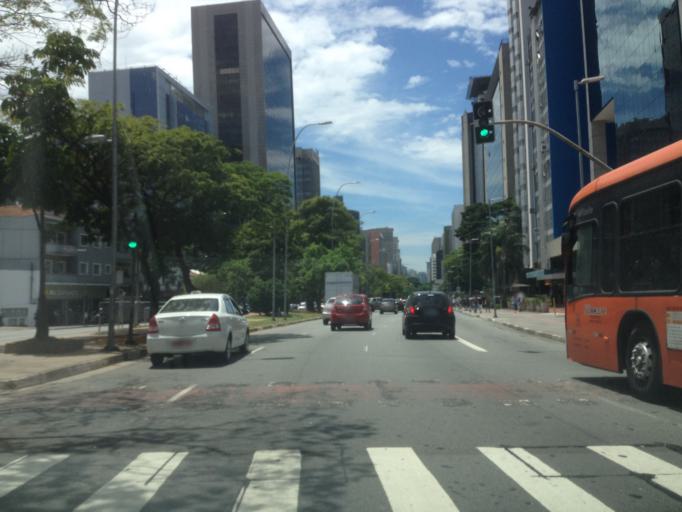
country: BR
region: Sao Paulo
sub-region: Sao Paulo
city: Sao Paulo
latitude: -23.5677
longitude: -46.6930
